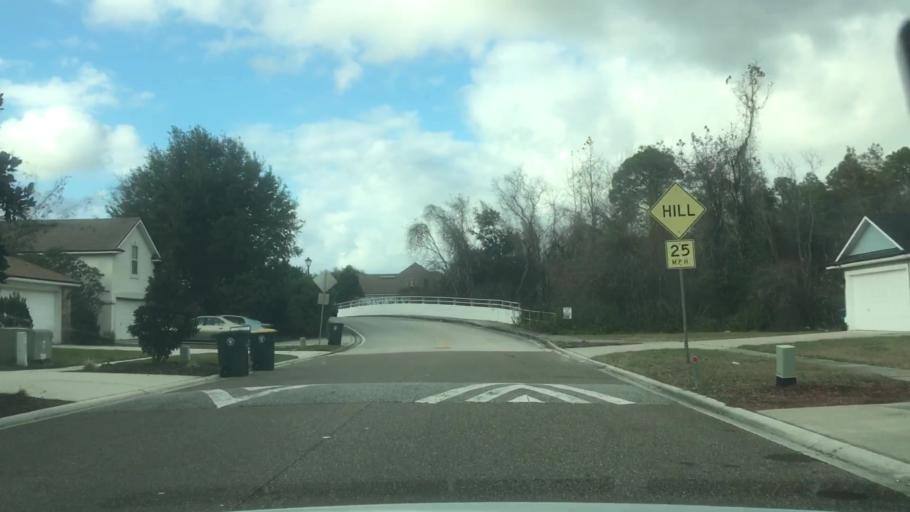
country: US
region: Florida
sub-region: Duval County
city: Neptune Beach
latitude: 30.3057
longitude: -81.5042
